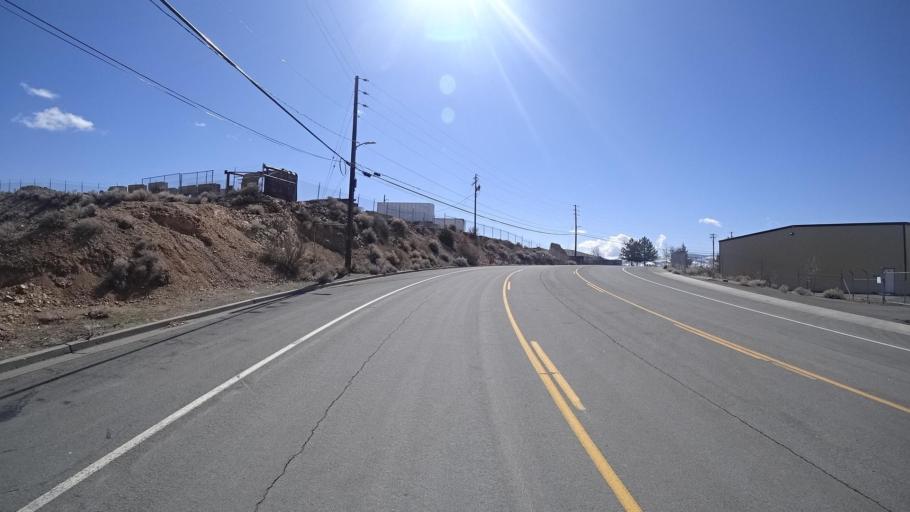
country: US
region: Nevada
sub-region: Washoe County
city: Golden Valley
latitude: 39.5931
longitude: -119.8330
